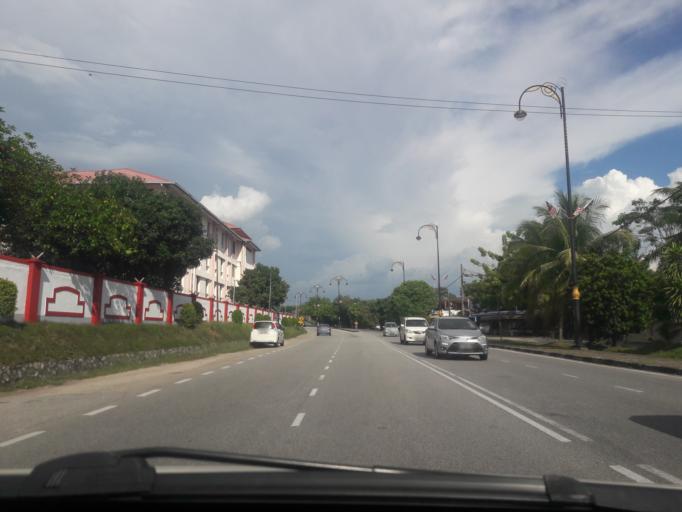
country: MY
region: Kedah
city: Sungai Petani
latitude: 5.6518
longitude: 100.5037
